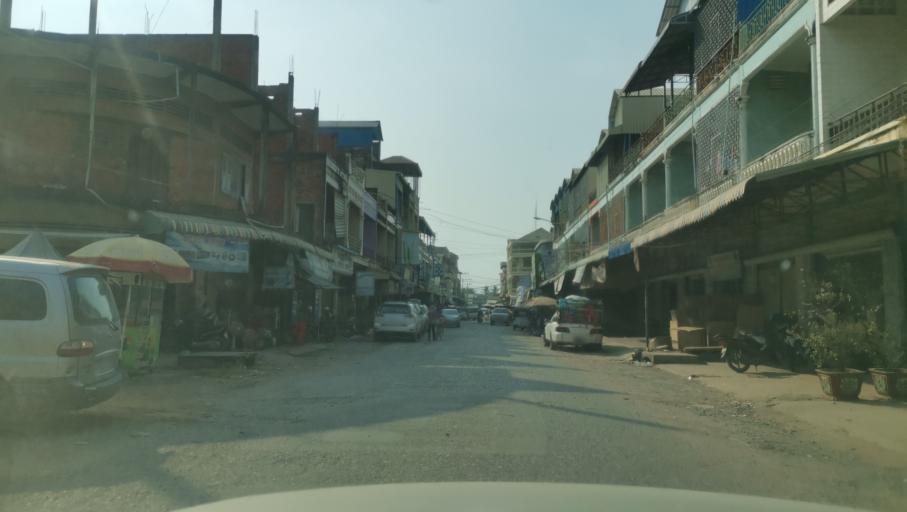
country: KH
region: Battambang
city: Battambang
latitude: 13.1041
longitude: 103.1949
